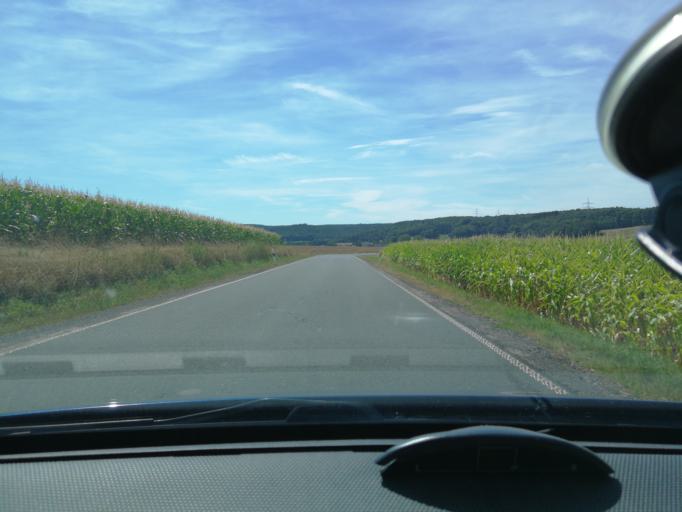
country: DE
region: Rheinland-Pfalz
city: Heidweiler
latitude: 49.9169
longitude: 6.7572
